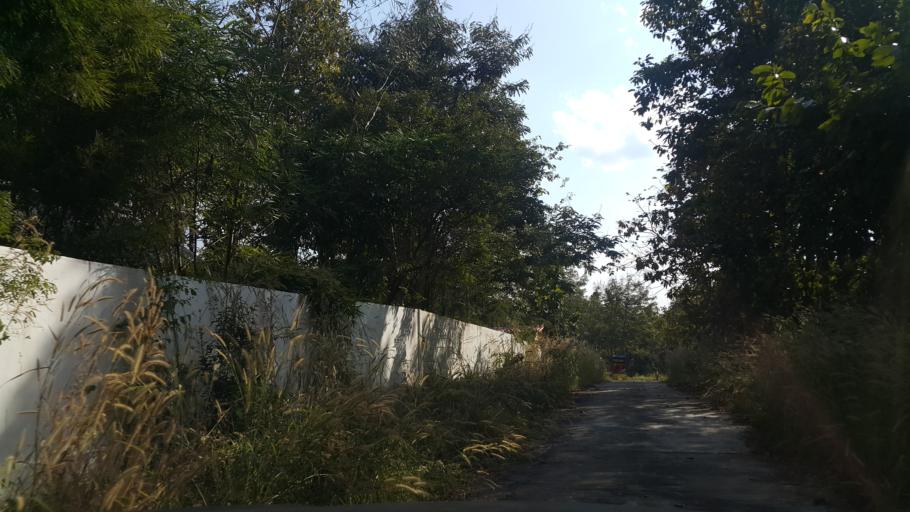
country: TH
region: Lamphun
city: Ban Thi
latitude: 18.5742
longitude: 99.1268
